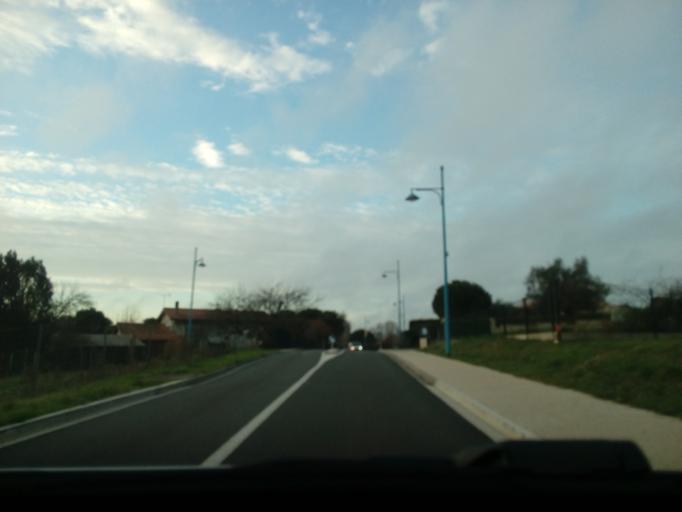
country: FR
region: Poitou-Charentes
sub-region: Departement de la Charente-Maritime
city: Jonzac
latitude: 45.4389
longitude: -0.4236
